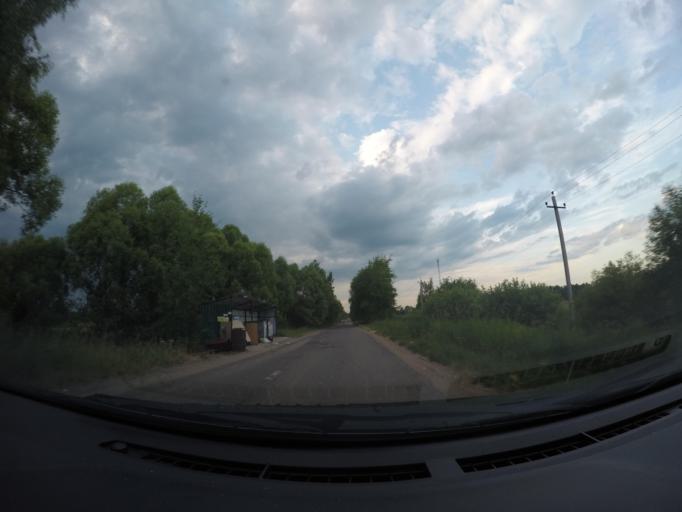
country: RU
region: Moskovskaya
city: Krasnyy Tkach
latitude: 55.4255
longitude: 39.2434
